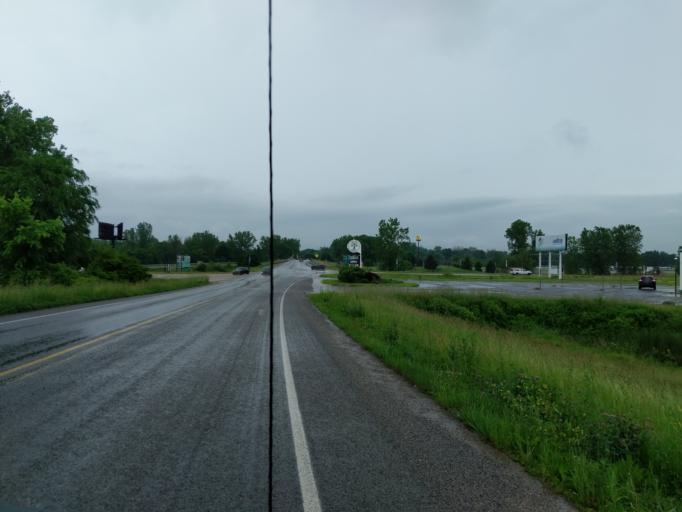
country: US
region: Michigan
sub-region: Berrien County
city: Coloma
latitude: 42.1735
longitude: -86.3062
